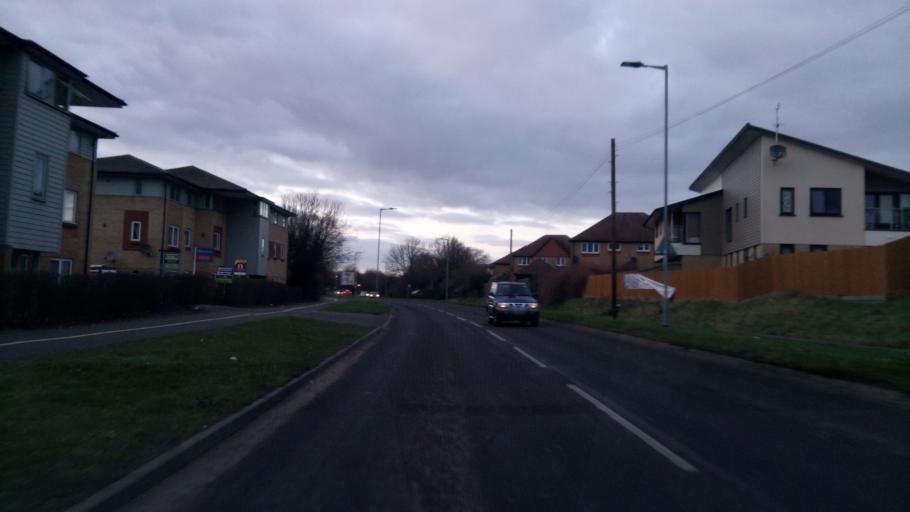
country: GB
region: England
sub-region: Peterborough
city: Peterborough
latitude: 52.5565
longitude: -0.2285
